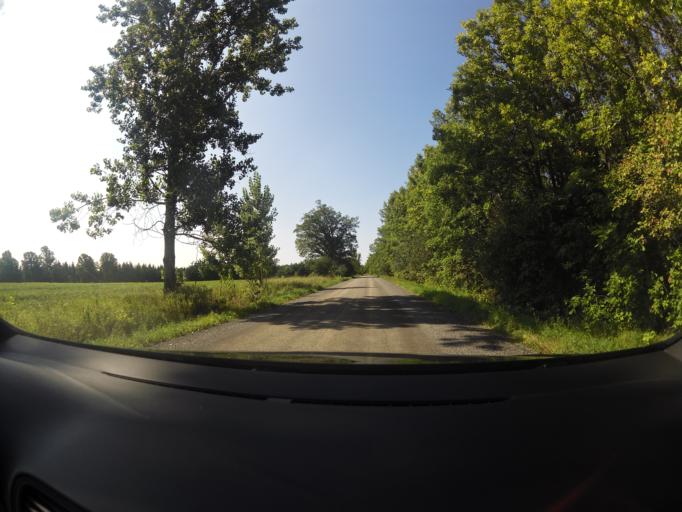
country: CA
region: Ontario
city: Arnprior
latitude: 45.3742
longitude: -76.2765
